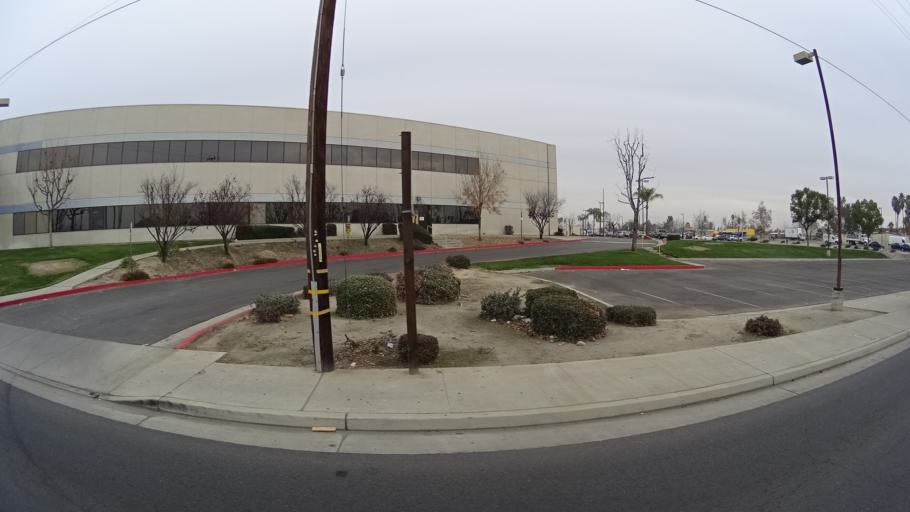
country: US
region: California
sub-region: Kern County
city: Bakersfield
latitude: 35.3693
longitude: -119.0028
